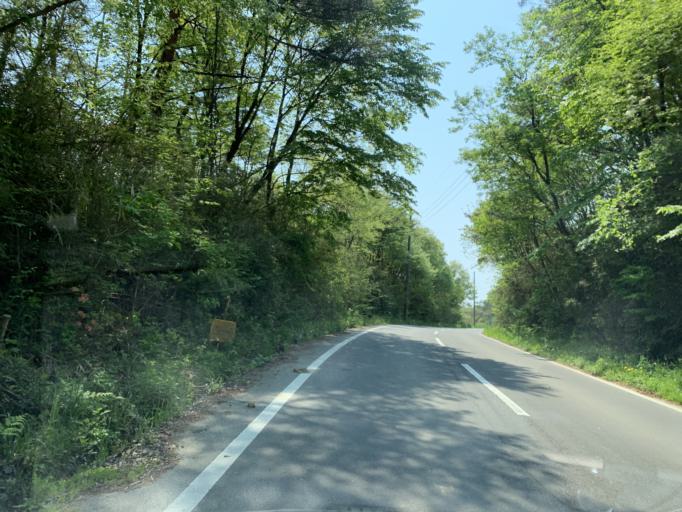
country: JP
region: Iwate
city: Ichinoseki
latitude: 38.8536
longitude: 141.0545
